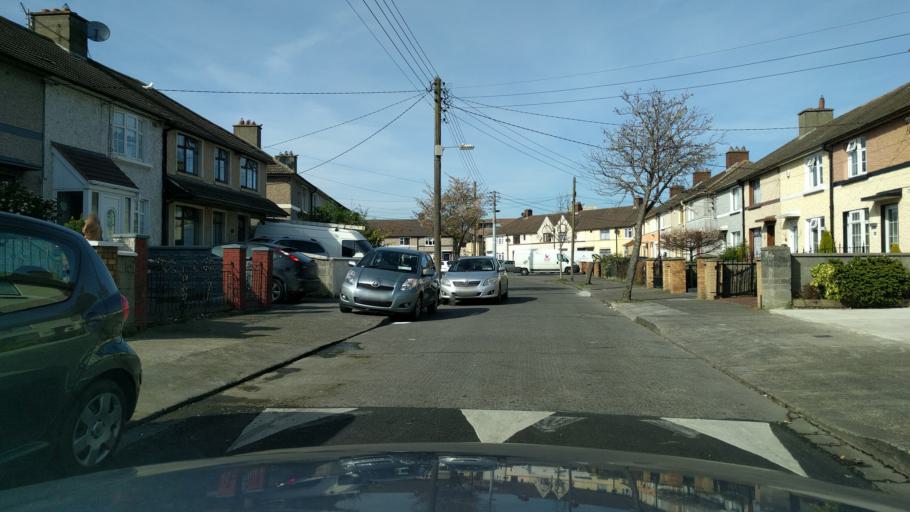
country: IE
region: Leinster
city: Chapelizod
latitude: 53.3408
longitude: -6.3499
